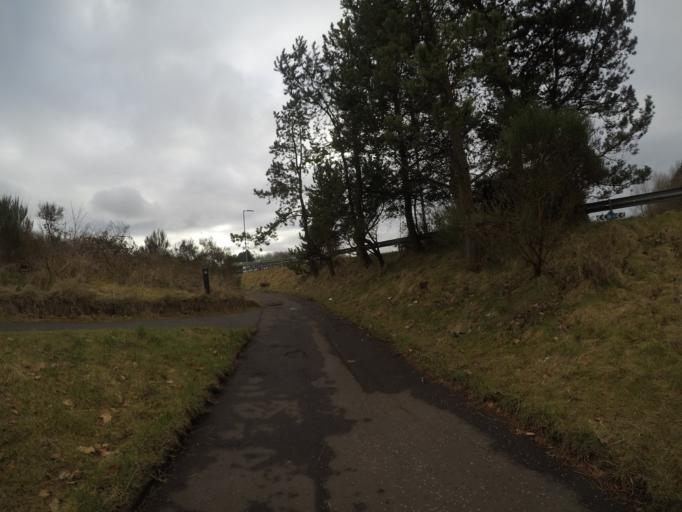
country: GB
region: Scotland
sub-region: North Ayrshire
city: Irvine
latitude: 55.6098
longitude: -4.6392
